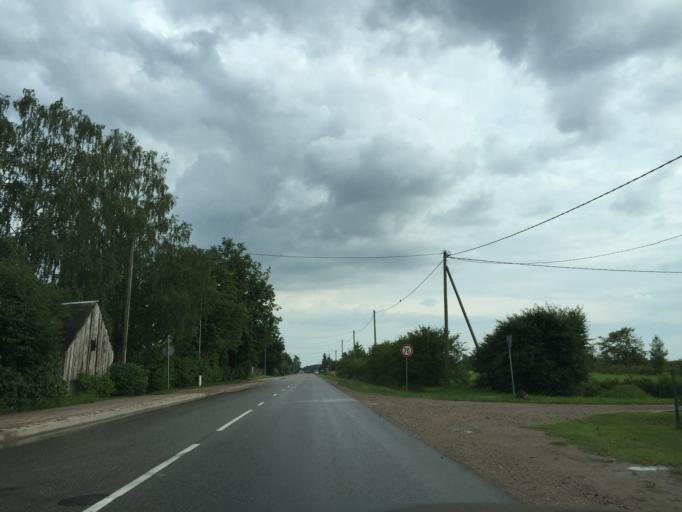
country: LV
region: Dobeles Rajons
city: Dobele
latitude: 56.6151
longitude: 23.2730
